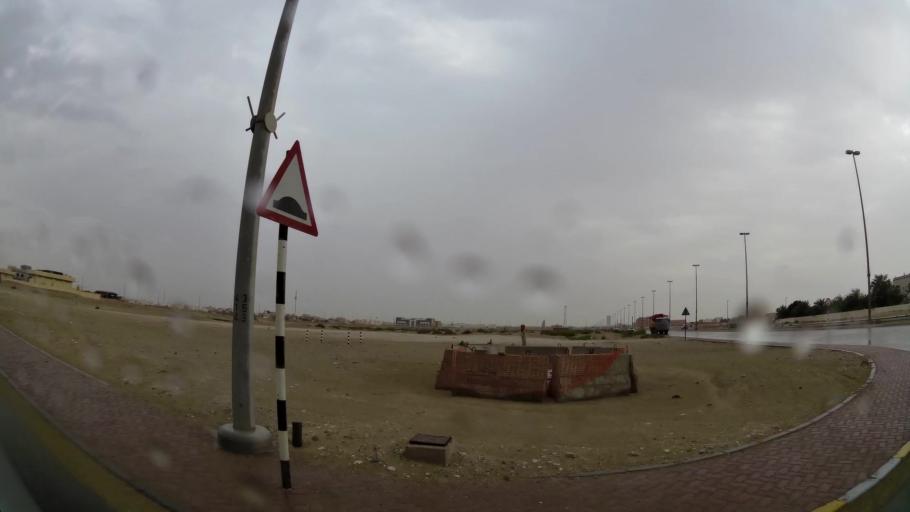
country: AE
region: Abu Dhabi
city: Abu Dhabi
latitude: 24.3660
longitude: 54.6283
